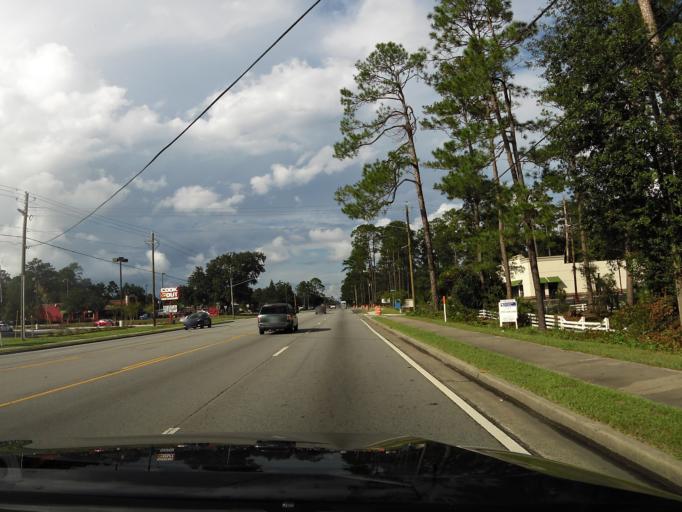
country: US
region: Georgia
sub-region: Liberty County
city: Hinesville
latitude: 31.8294
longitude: -81.5976
